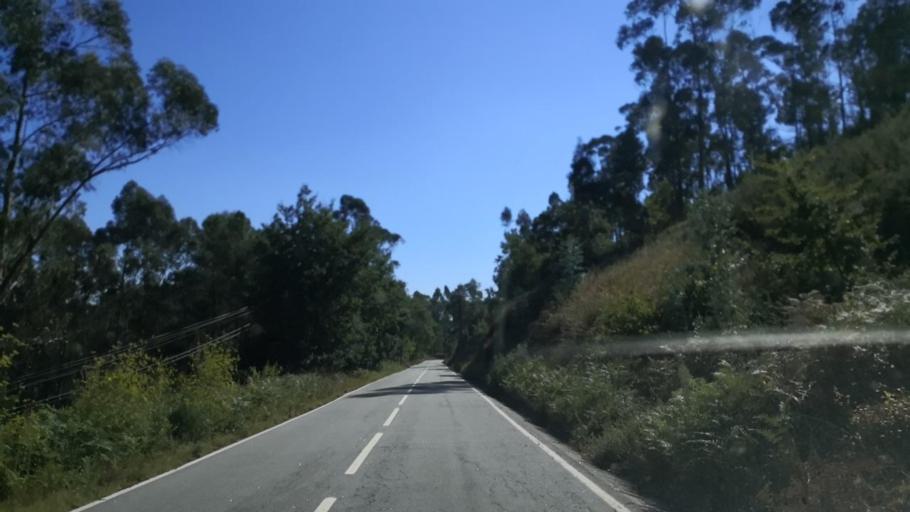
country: PT
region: Braga
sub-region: Fafe
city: Fafe
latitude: 41.4899
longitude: -8.1008
